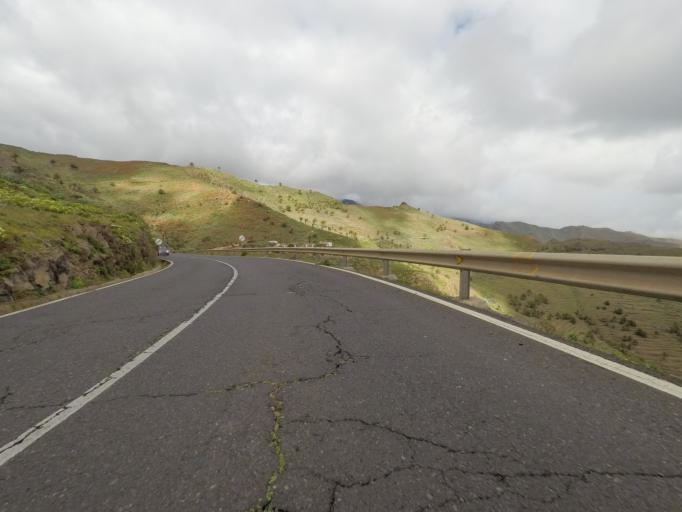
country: ES
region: Canary Islands
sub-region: Provincia de Santa Cruz de Tenerife
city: San Sebastian de la Gomera
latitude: 28.0962
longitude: -17.1712
